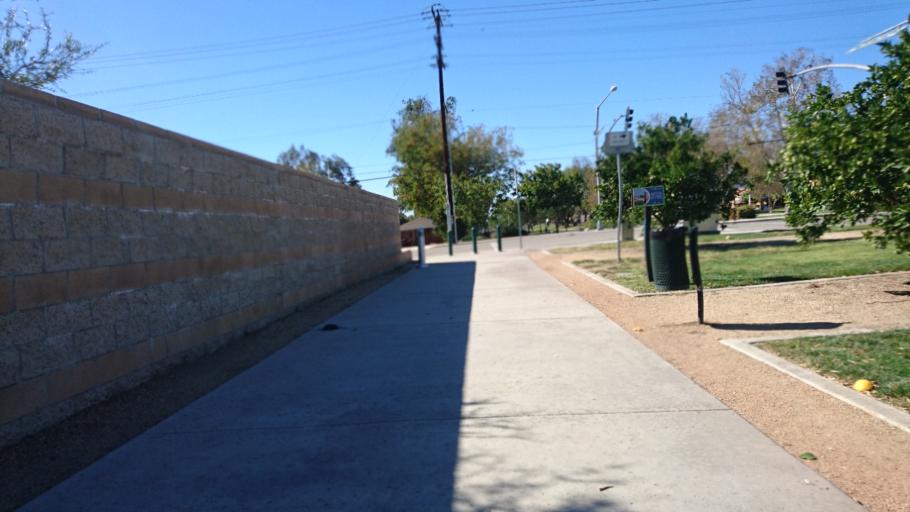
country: US
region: California
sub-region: San Bernardino County
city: Fontana
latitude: 34.1010
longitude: -117.4398
